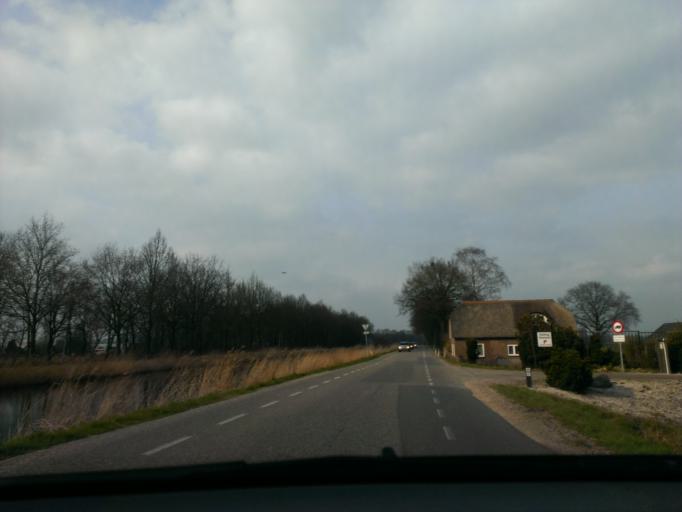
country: NL
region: Gelderland
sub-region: Gemeente Epe
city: Vaassen
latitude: 52.2938
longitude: 5.9982
